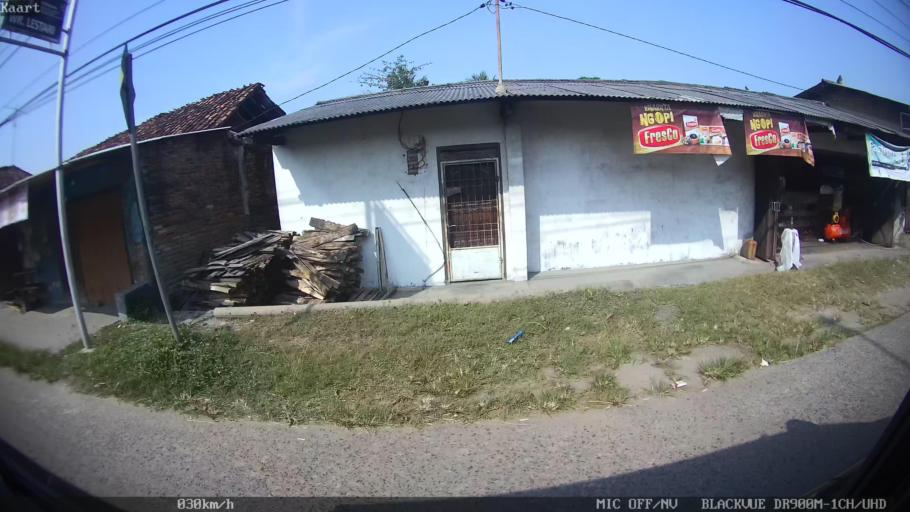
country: ID
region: Lampung
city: Natar
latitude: -5.2408
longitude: 105.1736
